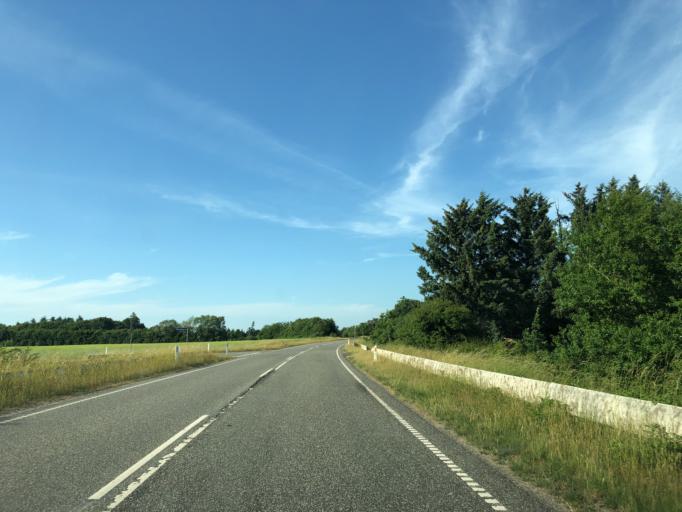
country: DK
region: Central Jutland
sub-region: Holstebro Kommune
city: Ulfborg
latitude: 56.3706
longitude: 8.4406
